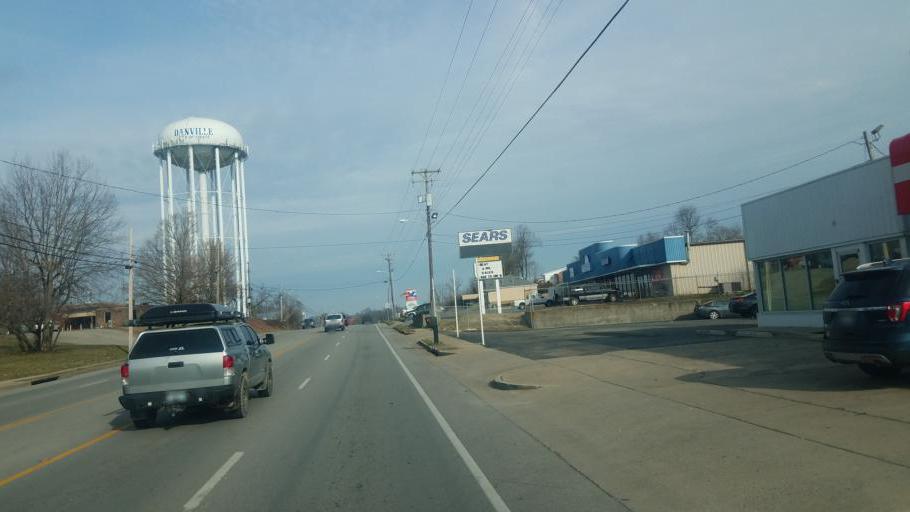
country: US
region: Kentucky
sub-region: Boyle County
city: Danville
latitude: 37.6317
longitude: -84.7748
